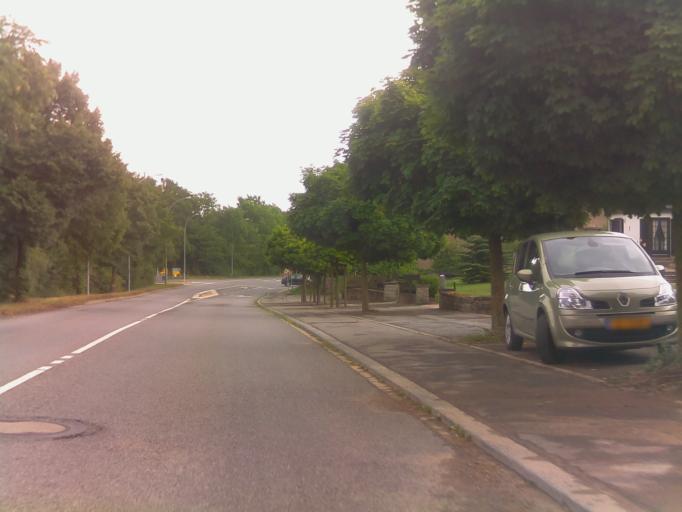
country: LU
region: Luxembourg
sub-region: Canton de Capellen
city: Dippach
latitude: 49.5779
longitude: 5.9893
